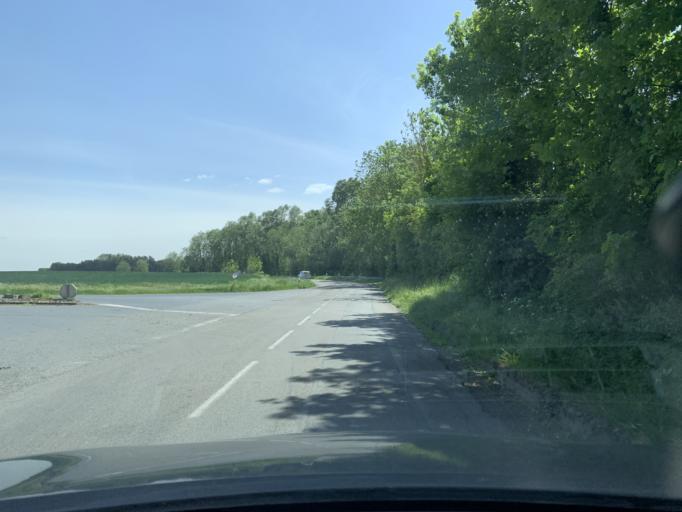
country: FR
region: Nord-Pas-de-Calais
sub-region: Departement du Nord
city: Marcoing
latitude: 50.1387
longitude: 3.1921
